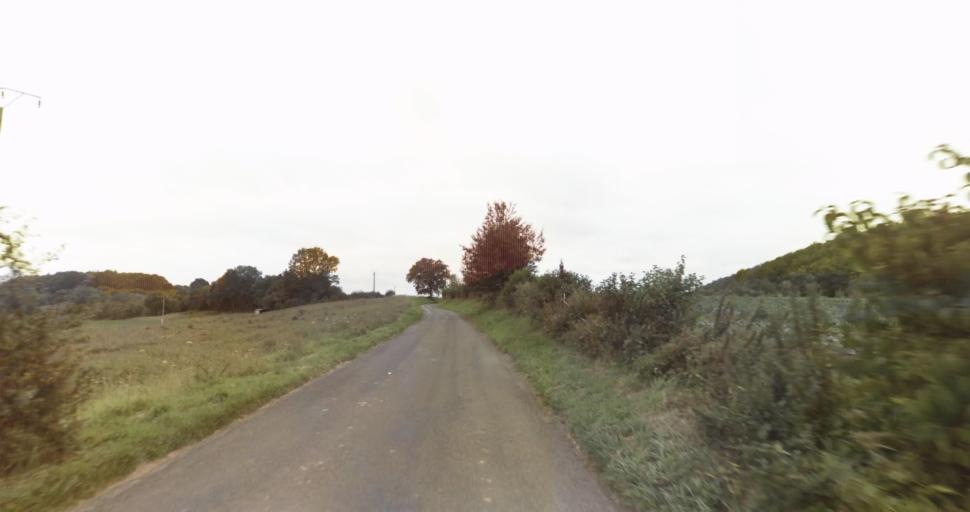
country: FR
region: Haute-Normandie
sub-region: Departement de l'Eure
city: Marcilly-sur-Eure
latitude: 48.8783
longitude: 1.3150
